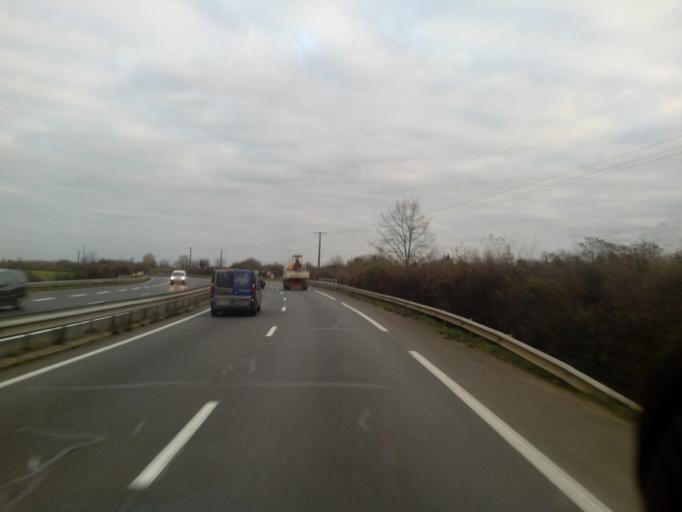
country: FR
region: Poitou-Charentes
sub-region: Departement de la Vienne
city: Chasseneuil-du-Poitou
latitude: 46.6144
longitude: 0.3659
